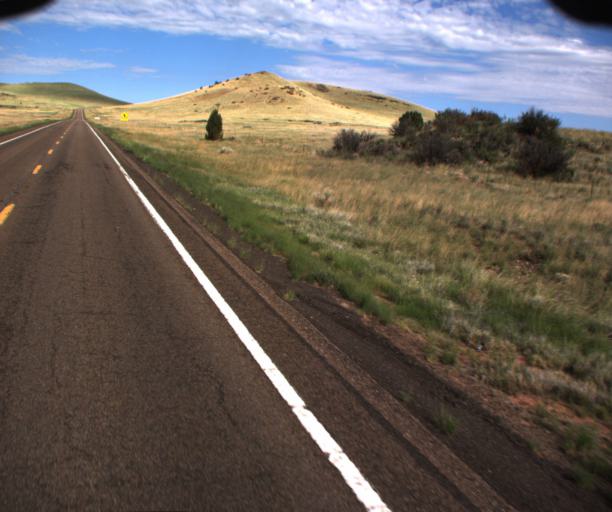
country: US
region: Arizona
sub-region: Apache County
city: Springerville
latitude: 34.2046
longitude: -109.4120
